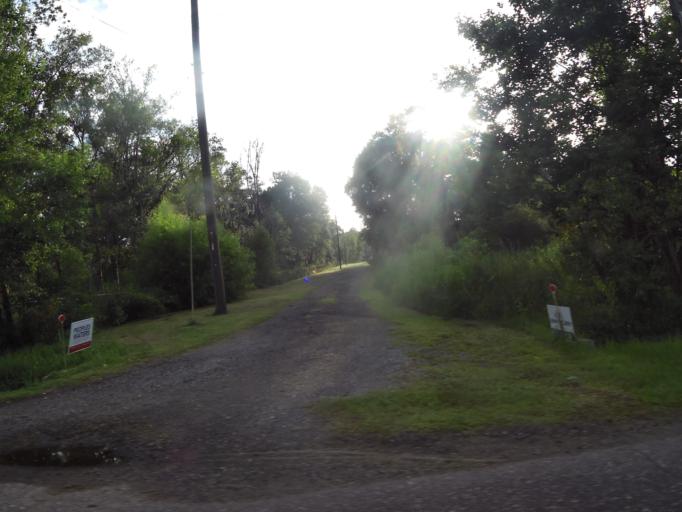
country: US
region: Florida
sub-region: Nassau County
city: Nassau Village-Ratliff
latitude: 30.3962
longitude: -81.7823
